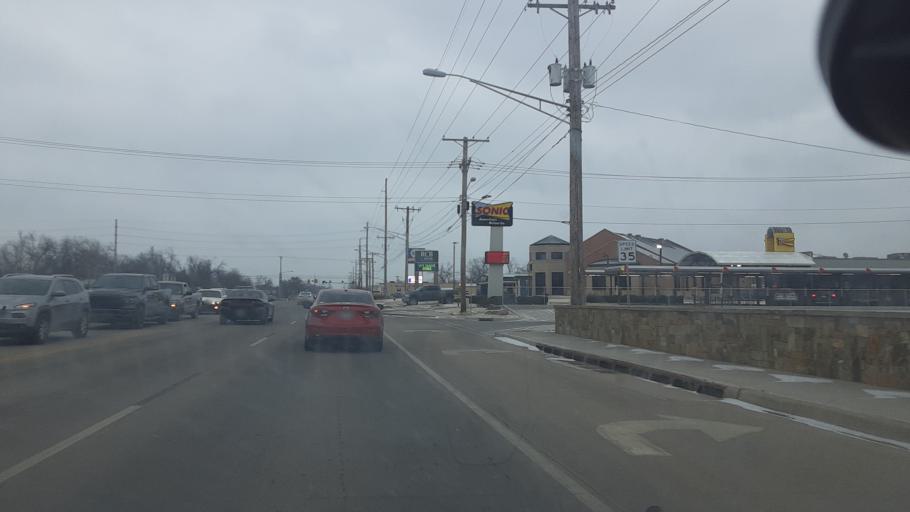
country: US
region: Oklahoma
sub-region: Payne County
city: Stillwater
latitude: 36.1166
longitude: -97.0513
